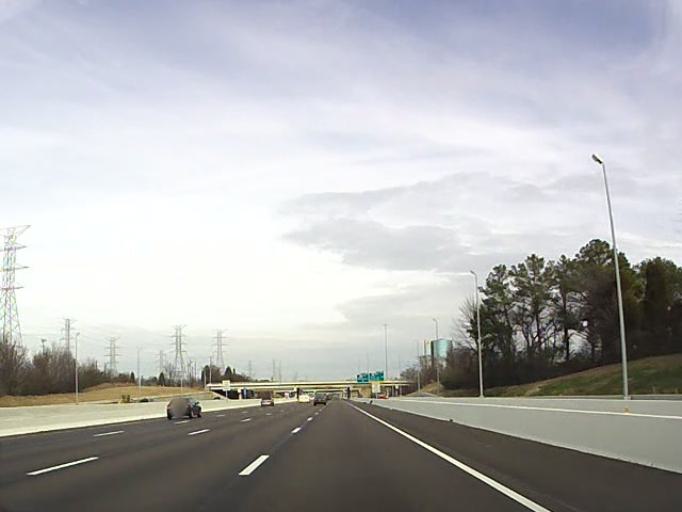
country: US
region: Tennessee
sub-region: Shelby County
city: Germantown
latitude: 35.0988
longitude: -89.8700
